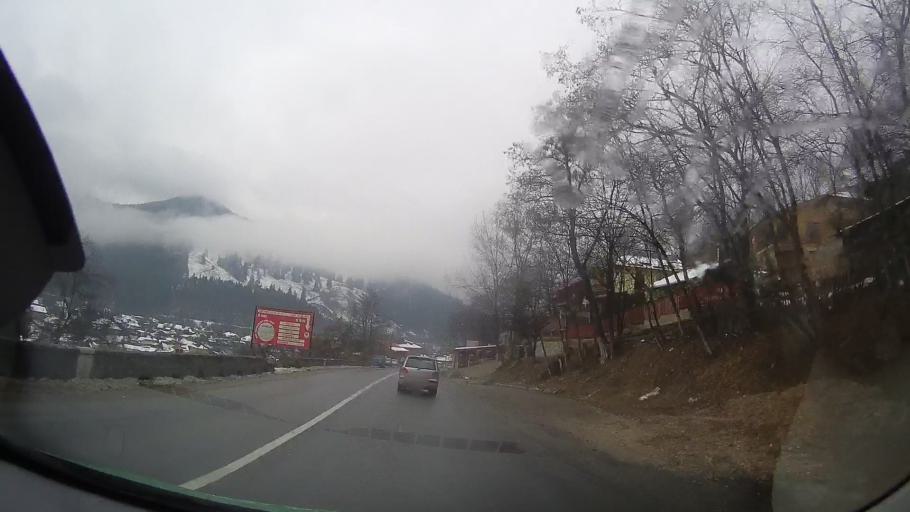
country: RO
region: Neamt
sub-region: Comuna Bicaz
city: Dodeni
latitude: 46.9027
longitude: 26.1139
